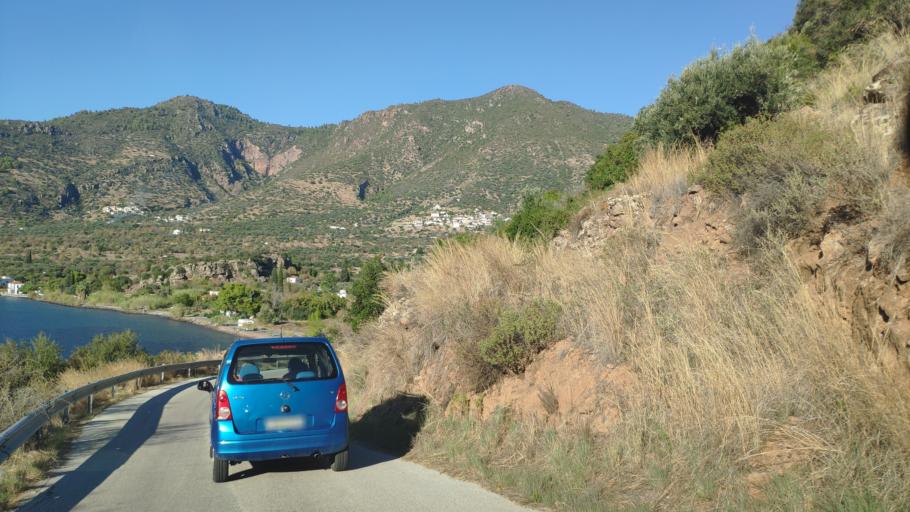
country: GR
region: Attica
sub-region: Nomos Piraios
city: Megalochori
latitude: 37.5822
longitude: 23.3485
